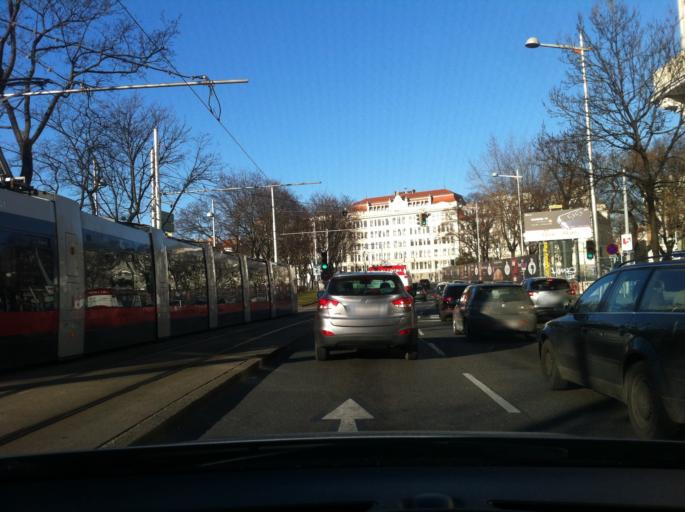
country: AT
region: Vienna
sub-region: Wien Stadt
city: Vienna
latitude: 48.1869
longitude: 16.3434
